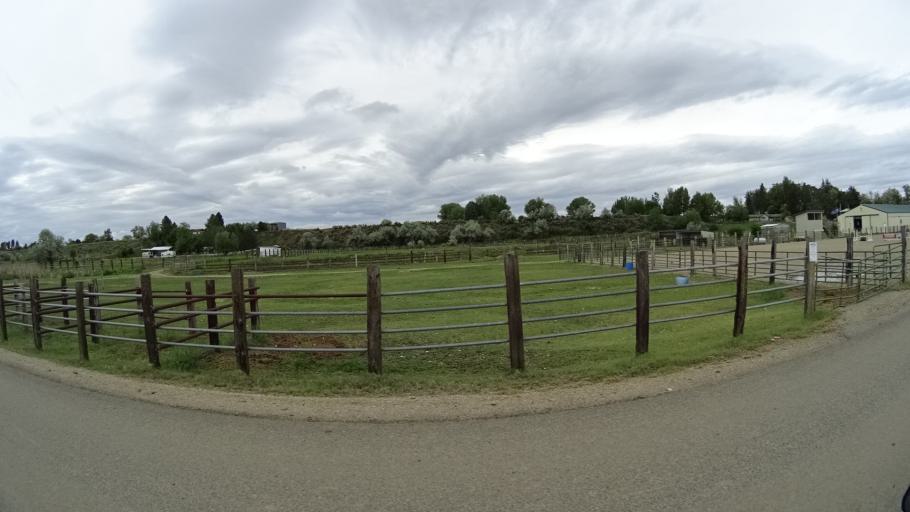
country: US
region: Idaho
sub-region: Ada County
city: Star
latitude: 43.6708
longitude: -116.5005
